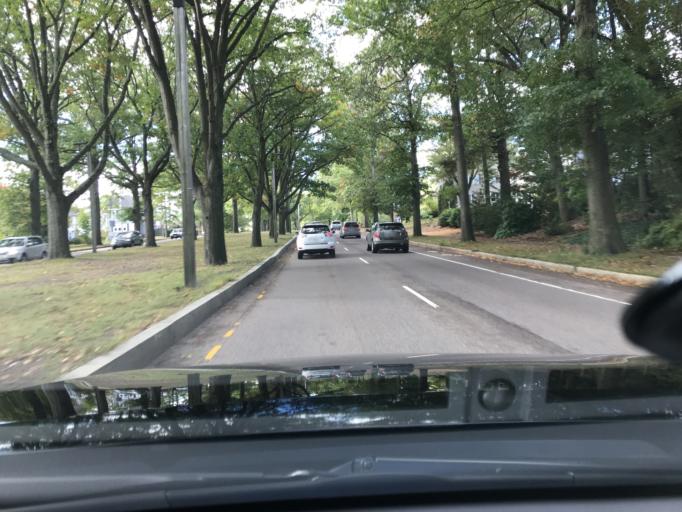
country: US
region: Massachusetts
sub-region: Norfolk County
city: Dedham
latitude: 42.2904
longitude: -71.1686
